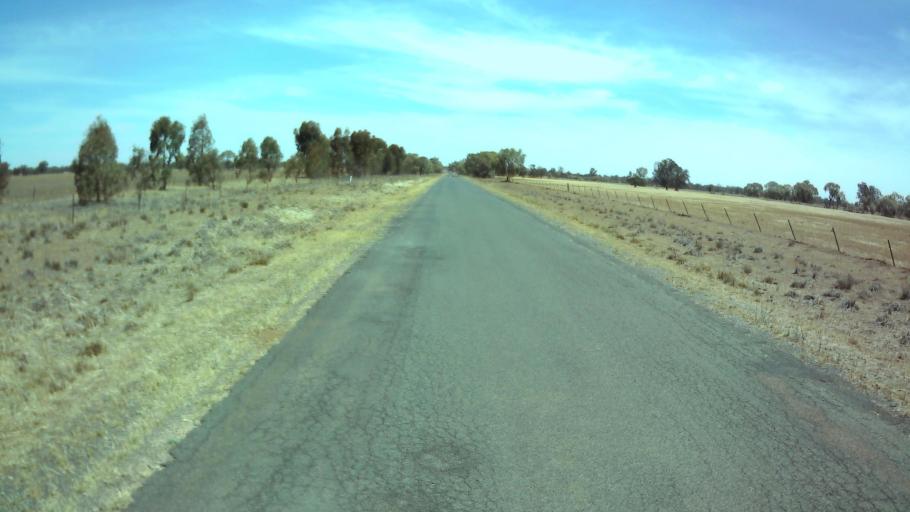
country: AU
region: New South Wales
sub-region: Weddin
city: Grenfell
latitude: -33.8231
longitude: 147.7471
